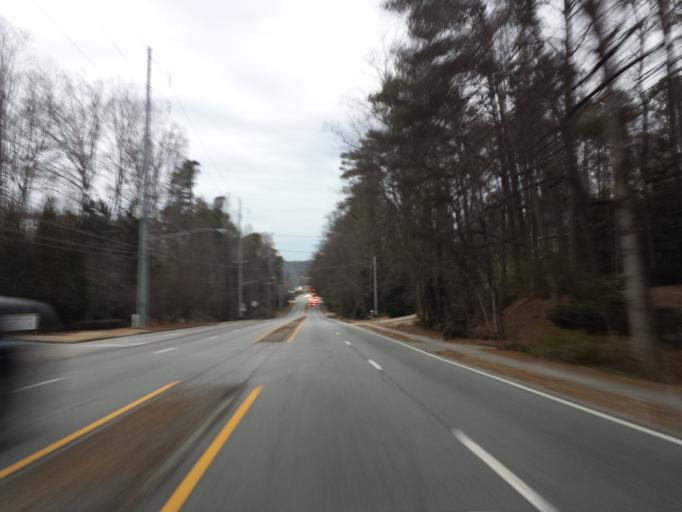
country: US
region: Georgia
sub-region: Cobb County
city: Vinings
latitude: 33.8416
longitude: -84.4212
